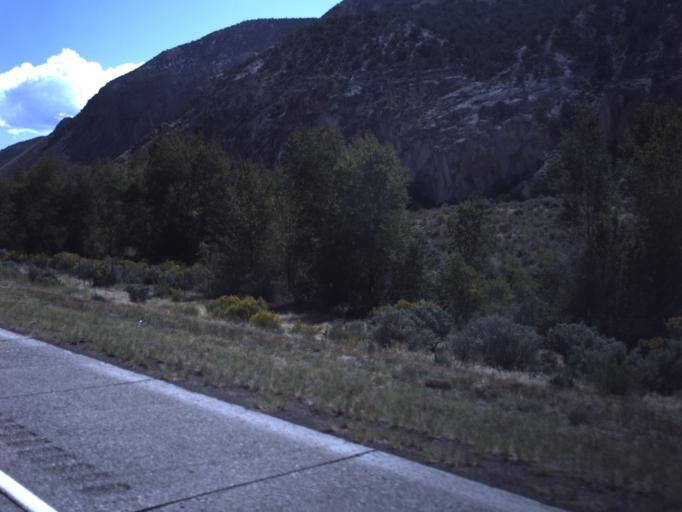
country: US
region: Utah
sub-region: Sevier County
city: Monroe
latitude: 38.5794
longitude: -112.3072
